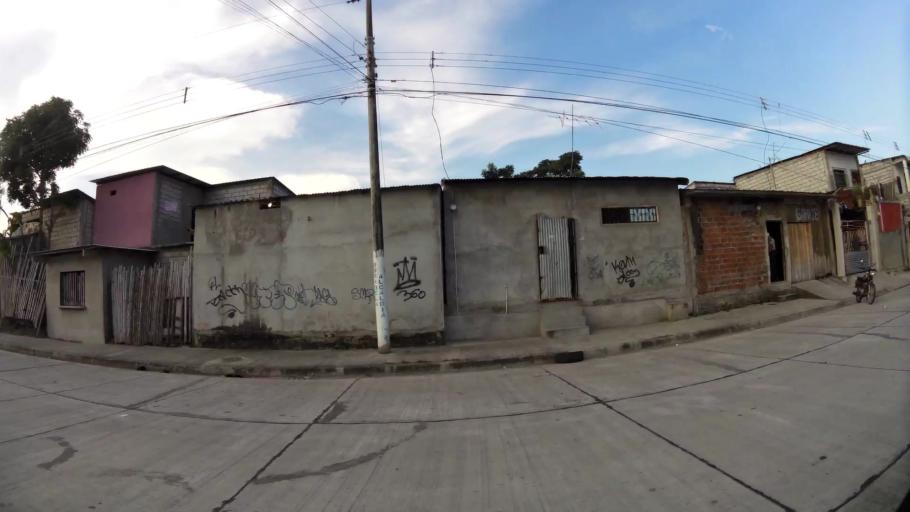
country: EC
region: Guayas
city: Eloy Alfaro
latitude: -2.0898
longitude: -79.8995
